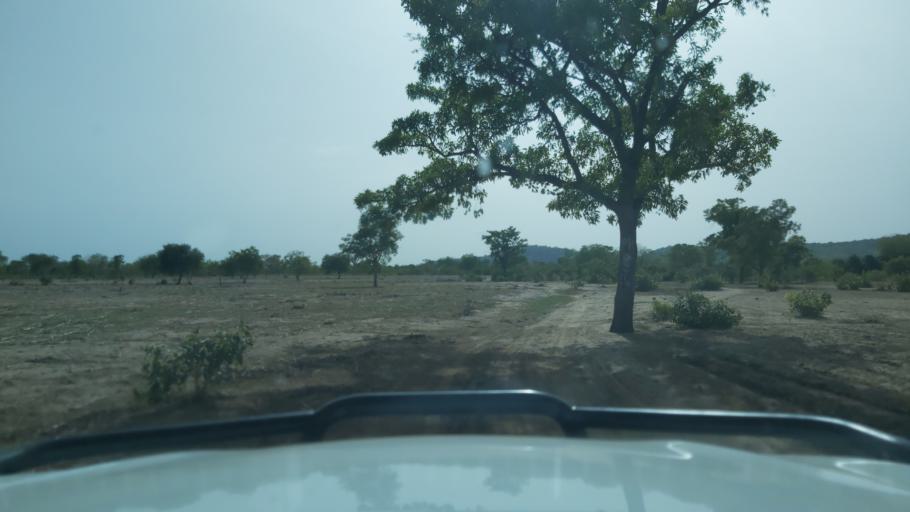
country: ML
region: Koulikoro
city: Koulikoro
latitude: 13.1755
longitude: -7.7476
